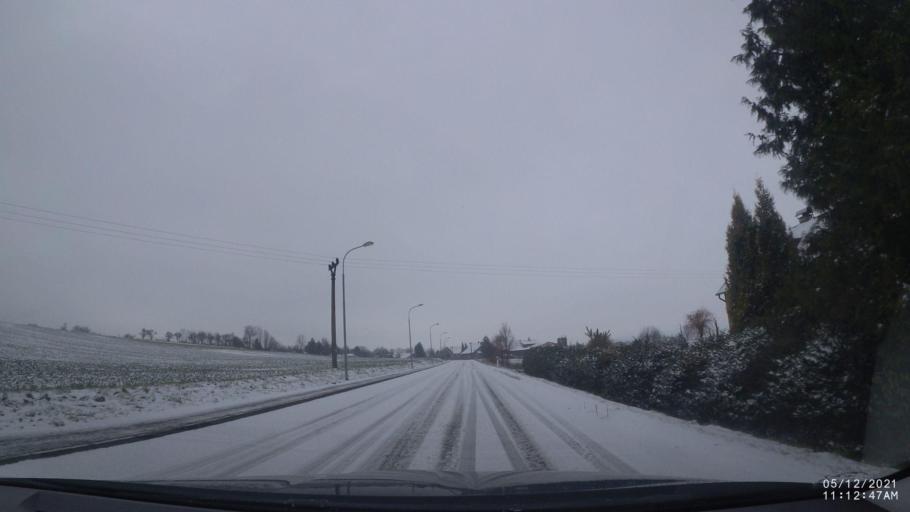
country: CZ
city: Solnice
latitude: 50.1832
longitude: 16.2236
